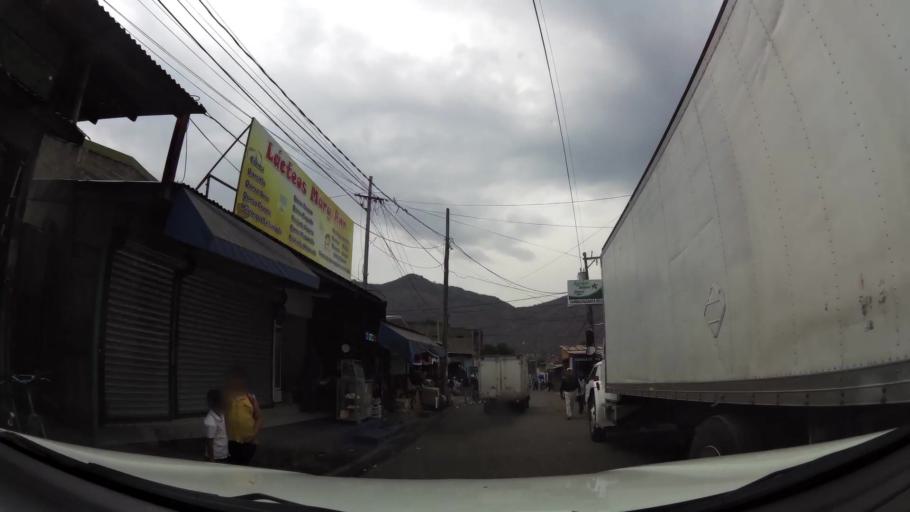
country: NI
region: Jinotega
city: Jinotega
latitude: 13.0947
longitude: -85.9975
